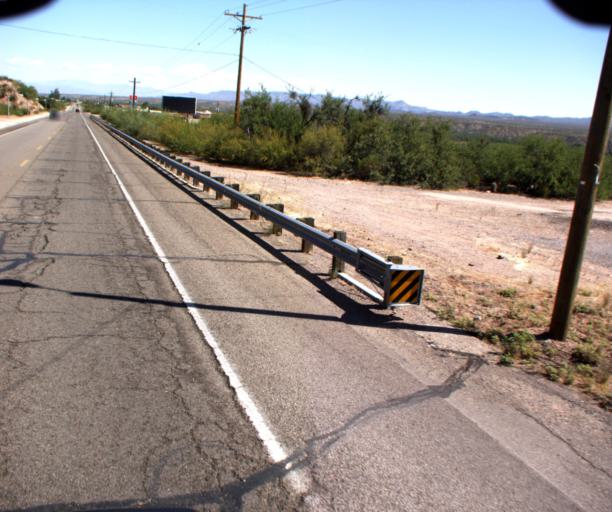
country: US
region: Arizona
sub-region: Pinal County
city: Mammoth
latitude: 32.7222
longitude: -110.6446
